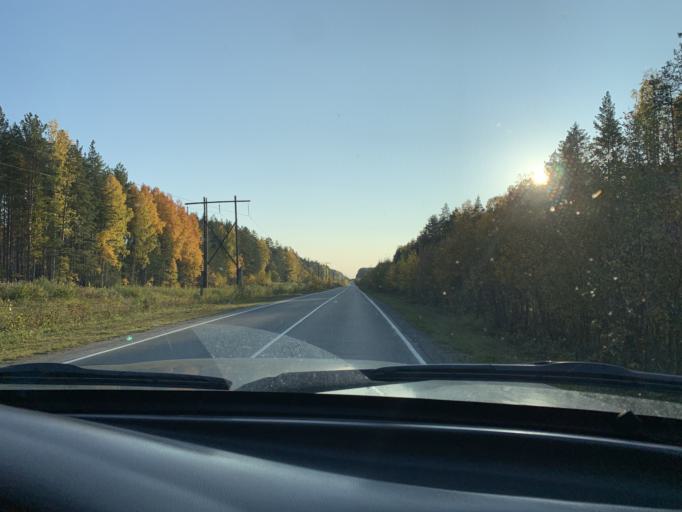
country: RU
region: Sverdlovsk
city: Verkhneye Dubrovo
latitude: 56.8774
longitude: 61.1158
